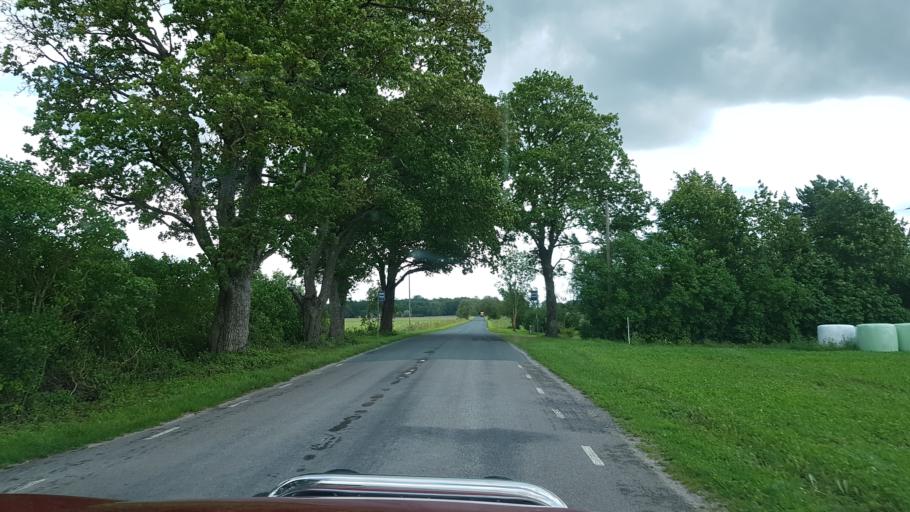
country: EE
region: Laeaene
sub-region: Lihula vald
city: Lihula
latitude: 58.7113
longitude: 24.0101
